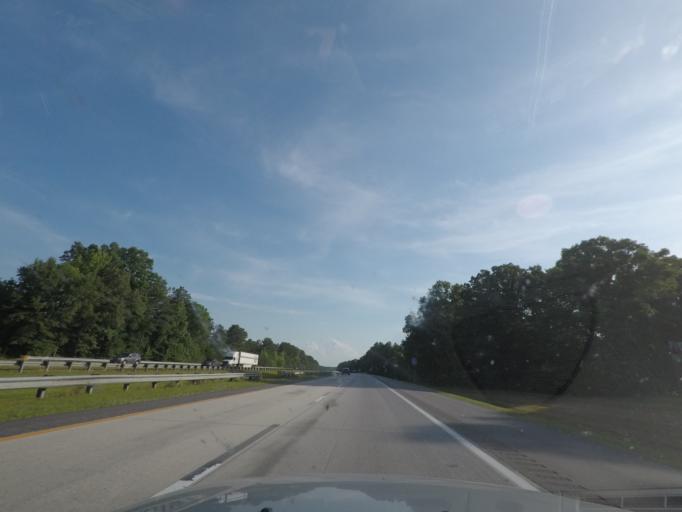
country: US
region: North Carolina
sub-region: Granville County
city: Oxford
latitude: 36.2654
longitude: -78.6130
